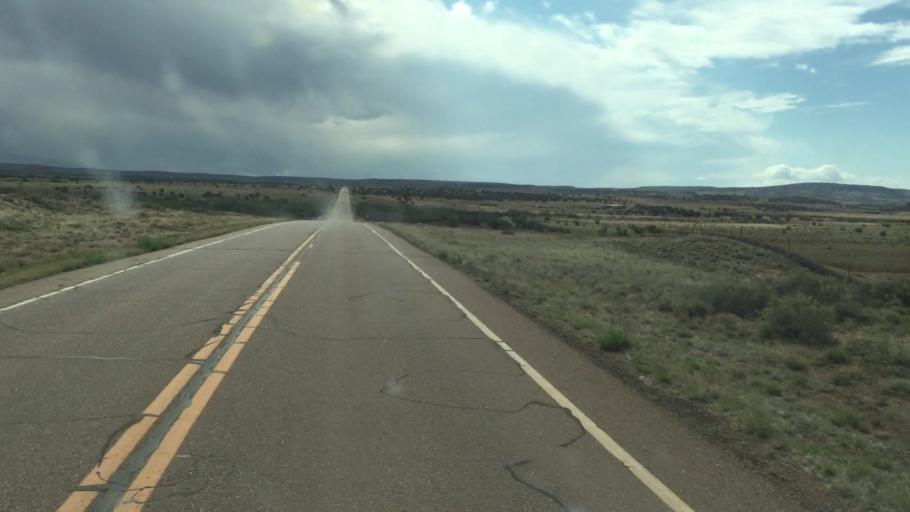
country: US
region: Arizona
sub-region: Navajo County
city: White Mountain Lake
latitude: 34.5159
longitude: -109.7027
